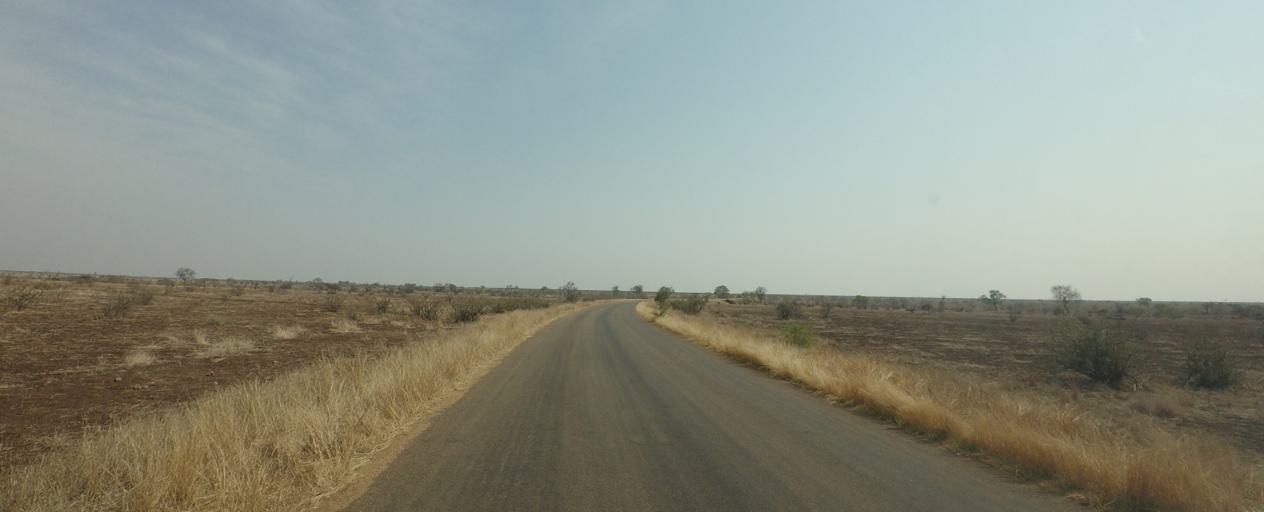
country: ZA
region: Limpopo
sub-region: Mopani District Municipality
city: Phalaborwa
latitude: -24.2696
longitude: 31.7302
